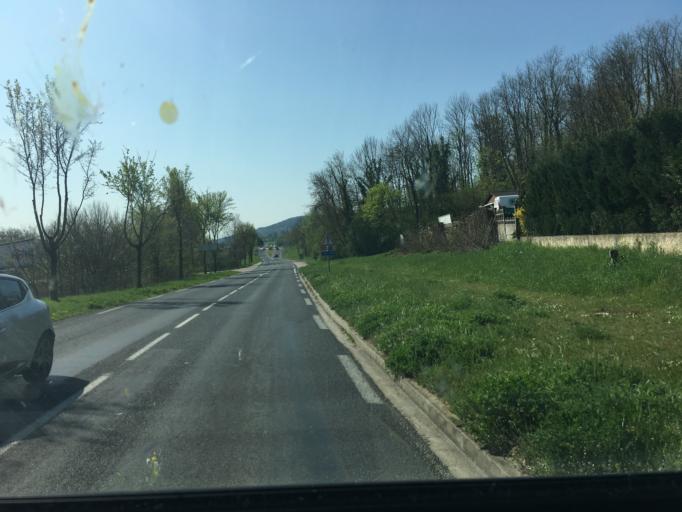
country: FR
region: Lorraine
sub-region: Departement de Meurthe-et-Moselle
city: Norroy-les-Pont-a-Mousson
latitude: 48.9216
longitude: 6.0382
